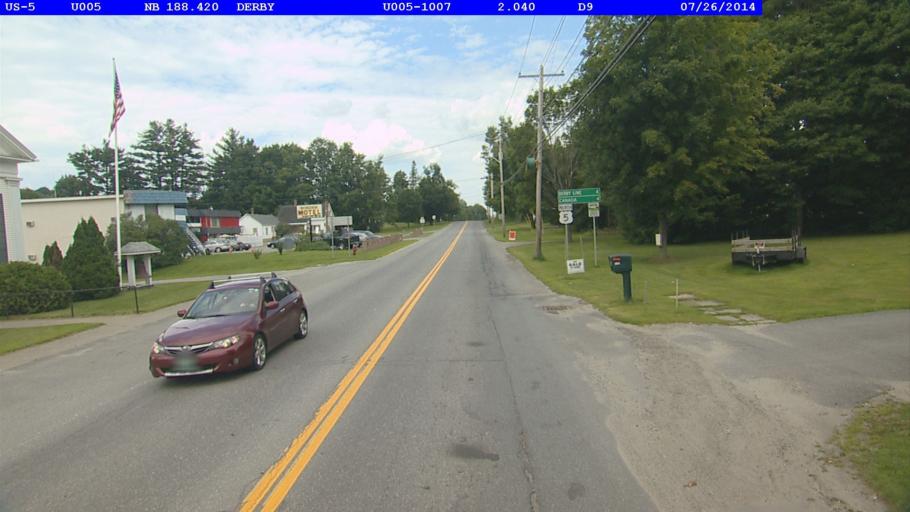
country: US
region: Vermont
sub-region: Orleans County
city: Newport
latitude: 44.9549
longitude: -72.1301
